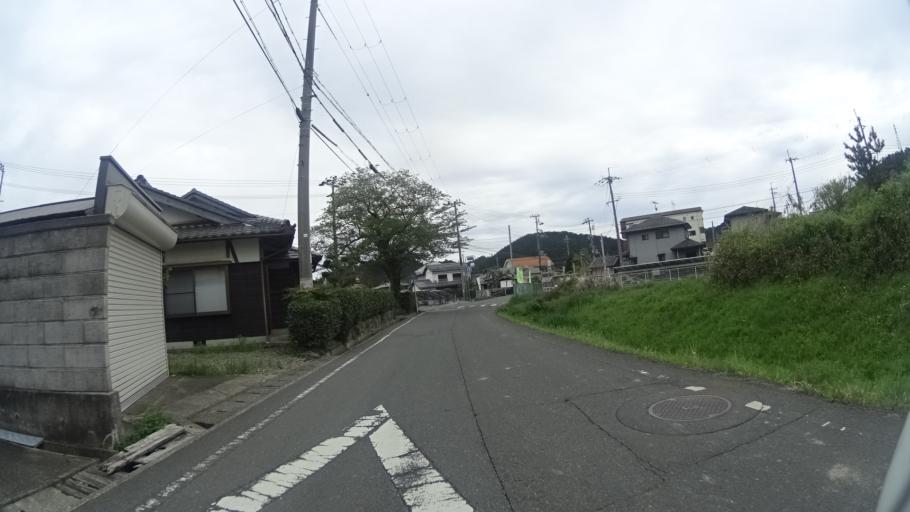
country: JP
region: Kyoto
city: Kameoka
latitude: 35.1979
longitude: 135.4638
